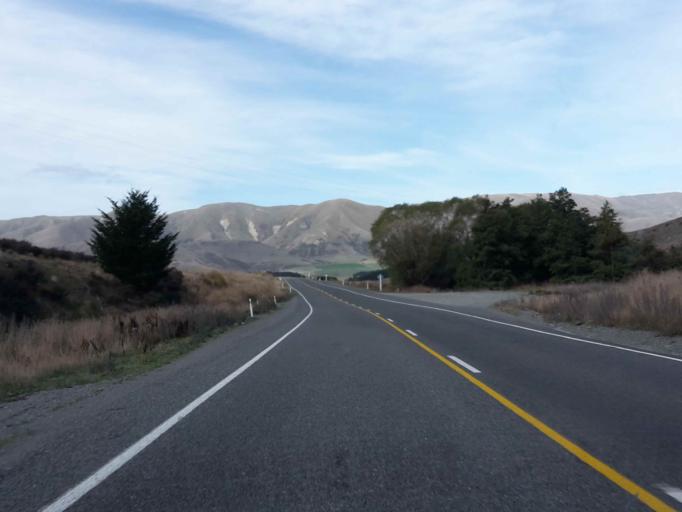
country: NZ
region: Canterbury
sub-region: Timaru District
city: Pleasant Point
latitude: -44.0912
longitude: 170.6134
